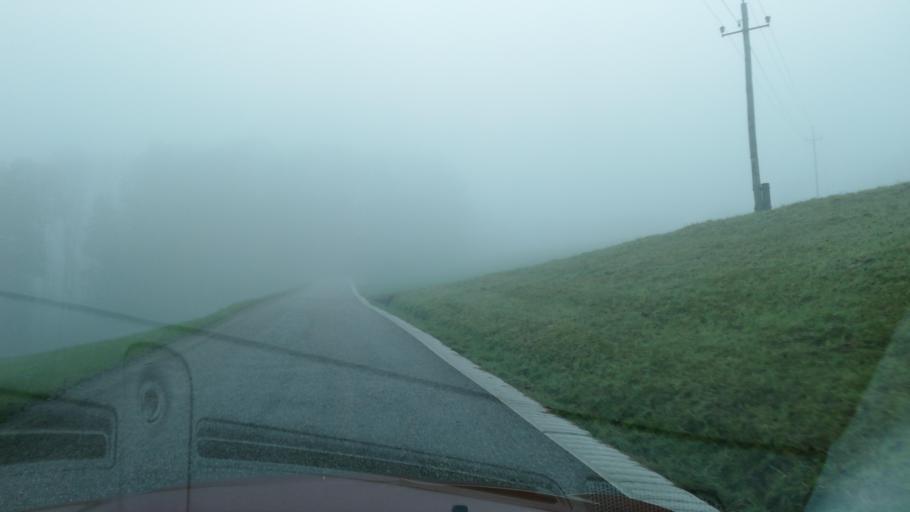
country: AT
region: Upper Austria
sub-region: Politischer Bezirk Grieskirchen
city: Bad Schallerbach
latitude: 48.2137
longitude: 13.8847
